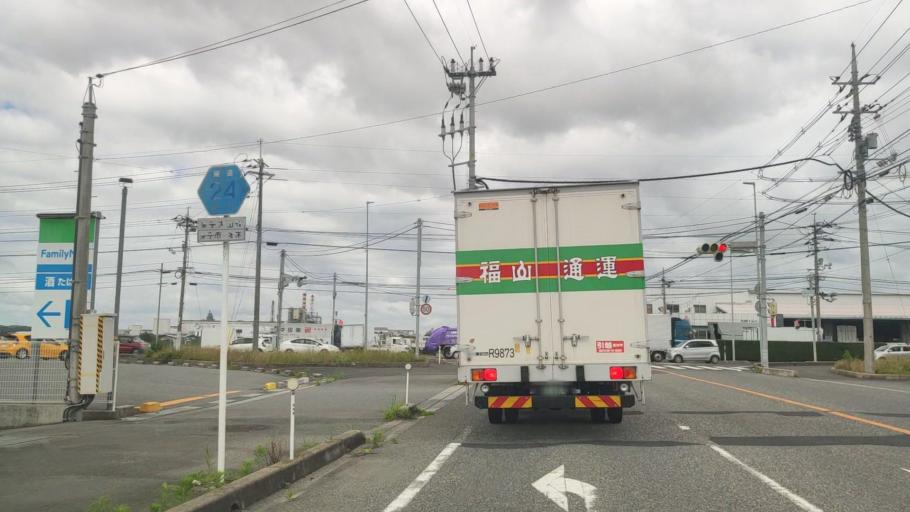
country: JP
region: Tottori
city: Yonago
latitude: 35.4357
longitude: 133.3883
